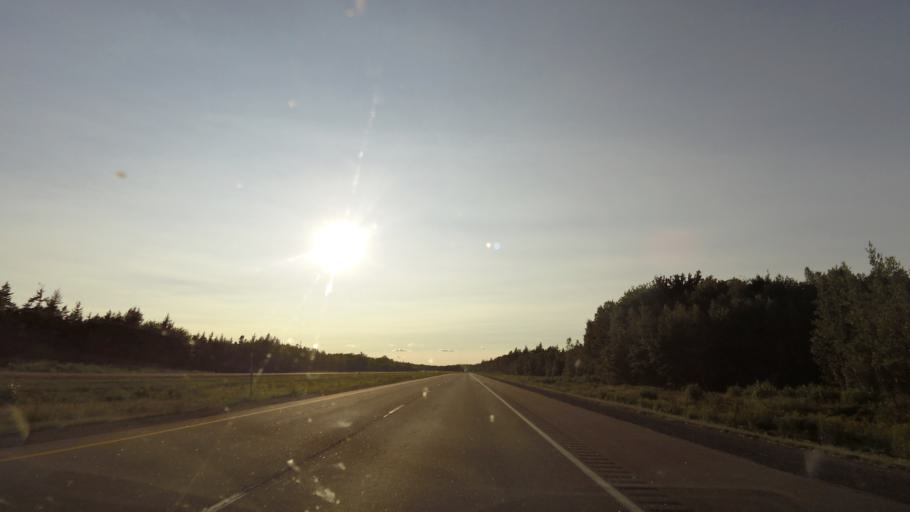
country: CA
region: New Brunswick
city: Dieppe
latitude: 46.1292
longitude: -64.6522
